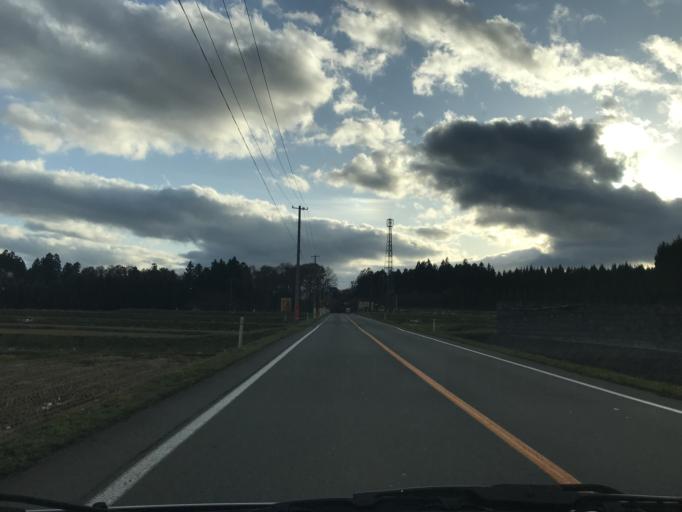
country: JP
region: Iwate
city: Mizusawa
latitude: 39.1734
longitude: 141.0449
